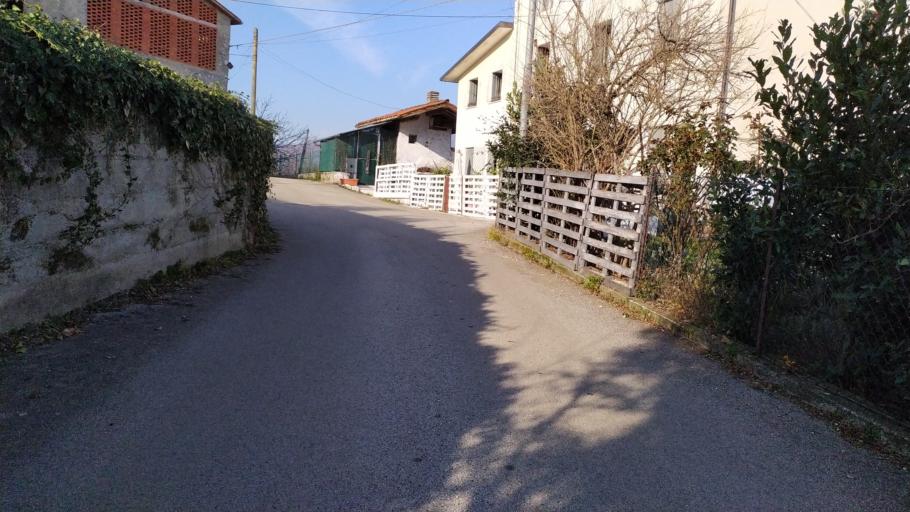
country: IT
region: Veneto
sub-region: Provincia di Vicenza
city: Monte di Malo
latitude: 45.6732
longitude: 11.3743
